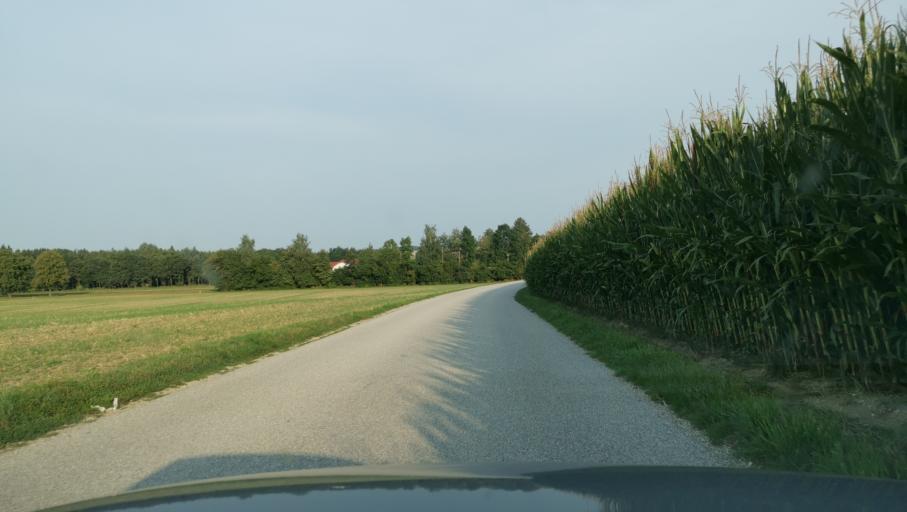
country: AT
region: Upper Austria
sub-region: Politischer Bezirk Grieskirchen
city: Grieskirchen
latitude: 48.2923
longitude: 13.8004
